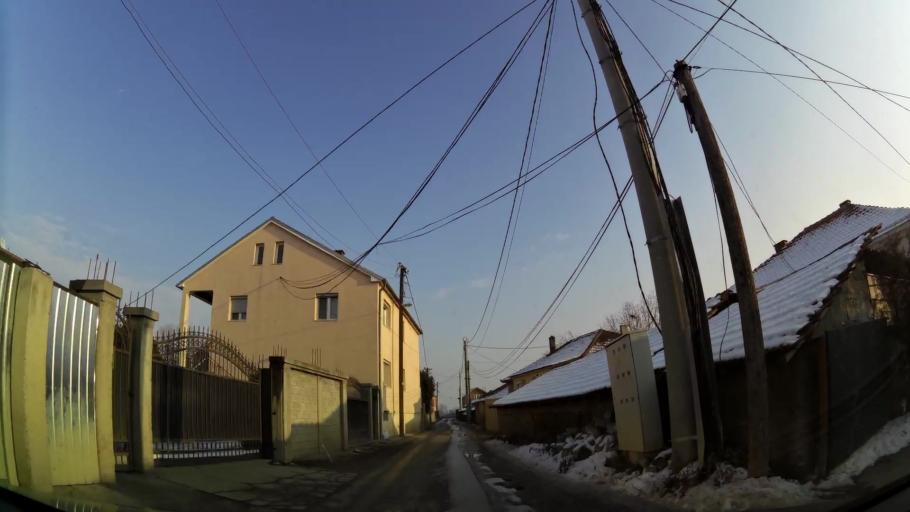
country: MK
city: Creshevo
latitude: 42.0175
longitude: 21.5219
